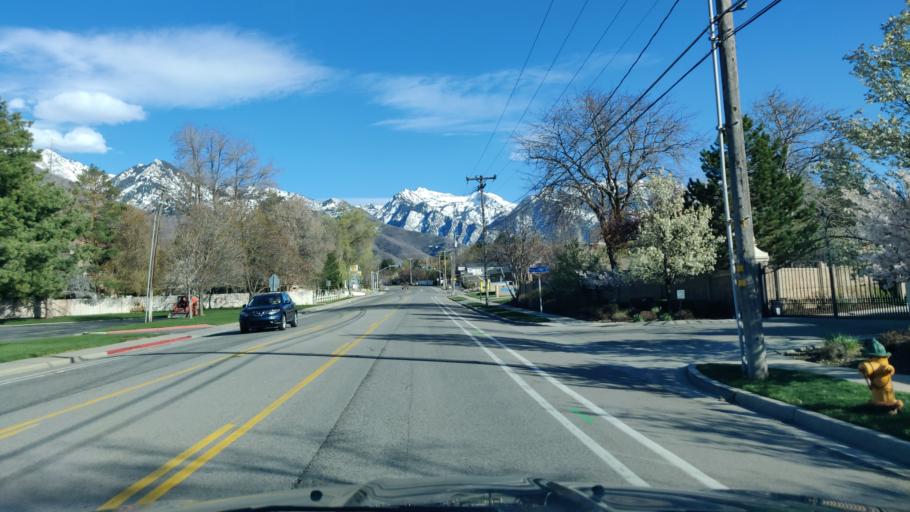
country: US
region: Utah
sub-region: Salt Lake County
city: Little Cottonwood Creek Valley
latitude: 40.6117
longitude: -111.8199
